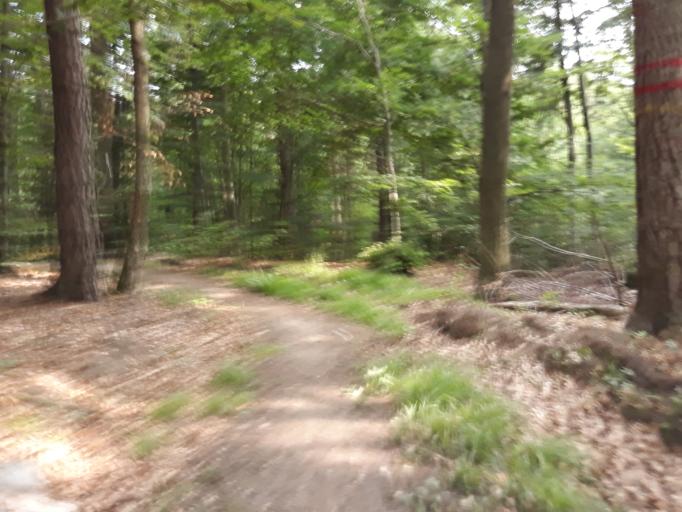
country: DE
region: Baden-Wuerttemberg
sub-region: Regierungsbezirk Stuttgart
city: Boeblingen
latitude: 48.6829
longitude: 9.0406
